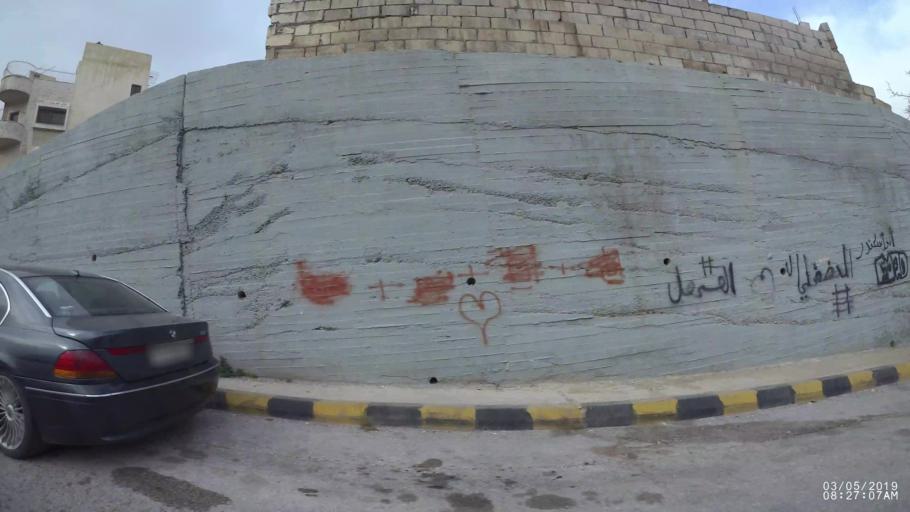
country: JO
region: Amman
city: Amman
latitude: 31.9616
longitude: 35.9344
